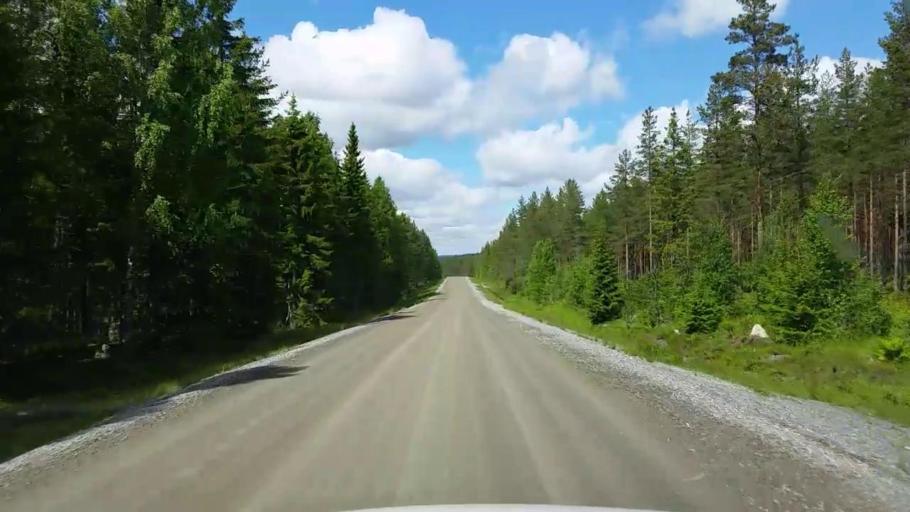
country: SE
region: Gaevleborg
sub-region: Bollnas Kommun
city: Vittsjo
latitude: 61.0498
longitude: 16.3317
